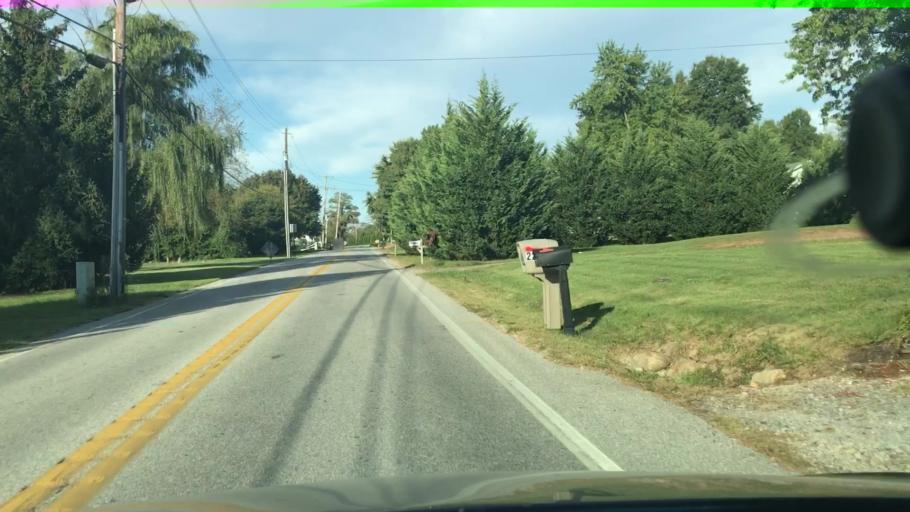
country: US
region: Pennsylvania
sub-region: York County
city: Weigelstown
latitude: 40.0181
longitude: -76.8075
